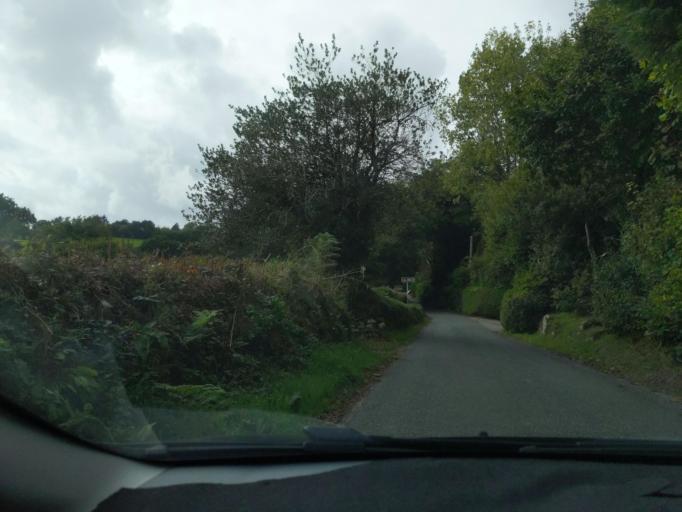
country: GB
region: England
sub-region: Cornwall
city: Lostwithiel
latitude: 50.4015
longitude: -4.6967
